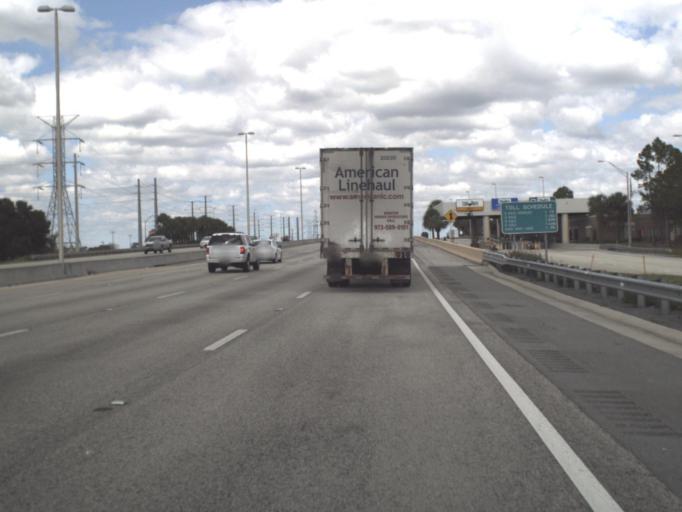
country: US
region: Florida
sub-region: Orange County
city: Tangelo Park
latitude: 28.4752
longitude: -81.4464
